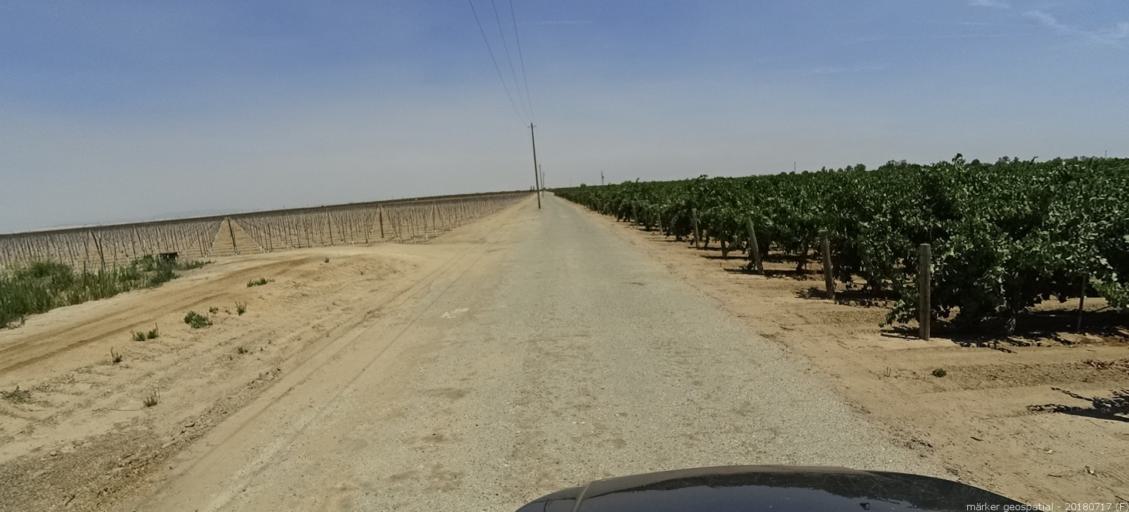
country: US
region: California
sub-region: Madera County
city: Fairmead
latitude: 37.0690
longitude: -120.1212
